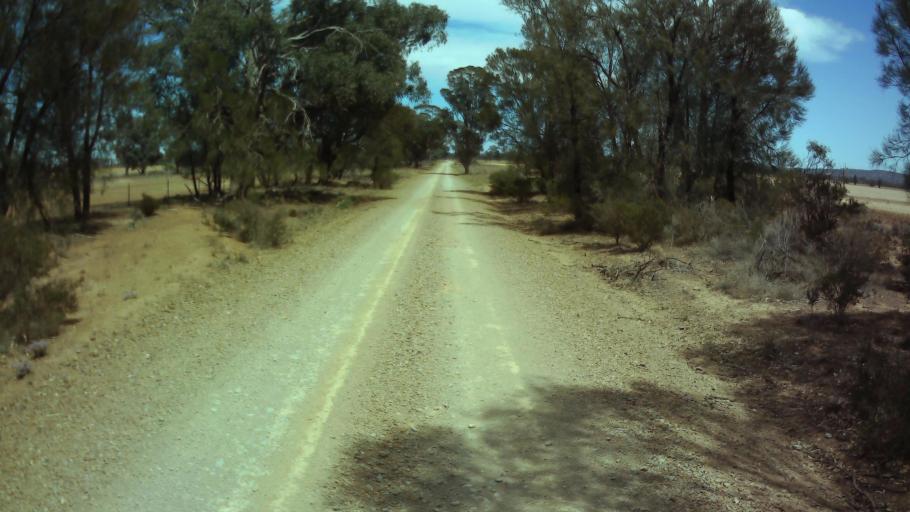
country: AU
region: New South Wales
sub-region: Weddin
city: Grenfell
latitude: -33.8572
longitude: 147.9130
